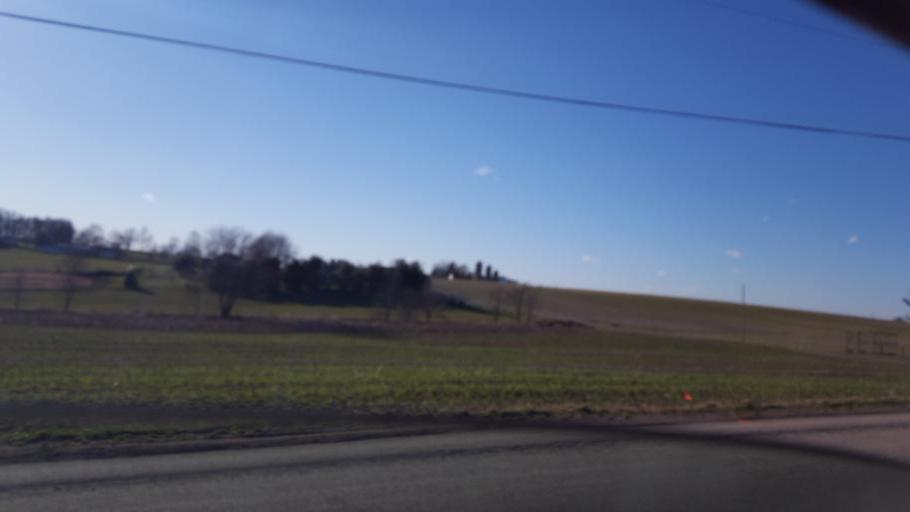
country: US
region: Ohio
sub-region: Holmes County
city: Millersburg
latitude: 40.6071
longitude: -81.7805
